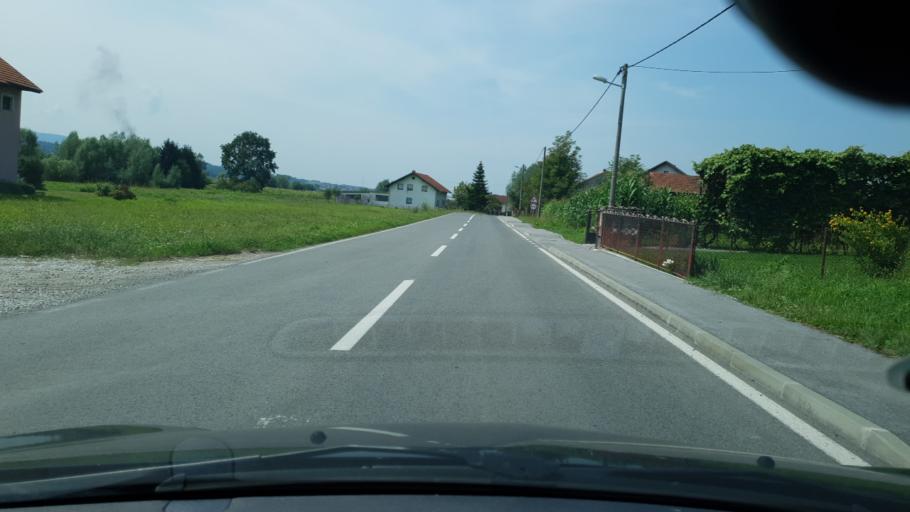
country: HR
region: Krapinsko-Zagorska
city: Bedekovcina
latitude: 46.0309
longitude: 15.9674
